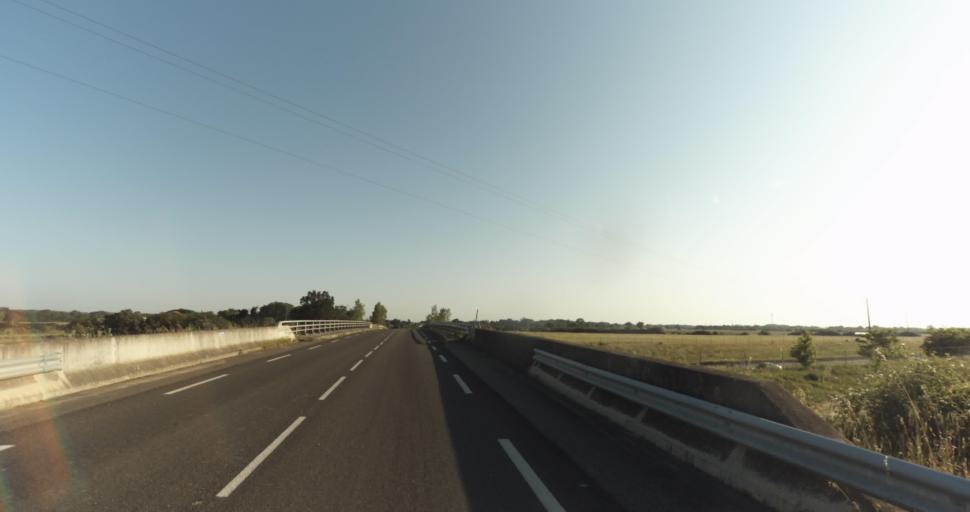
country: FR
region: Midi-Pyrenees
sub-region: Departement de la Haute-Garonne
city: Leguevin
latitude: 43.5809
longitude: 1.2364
